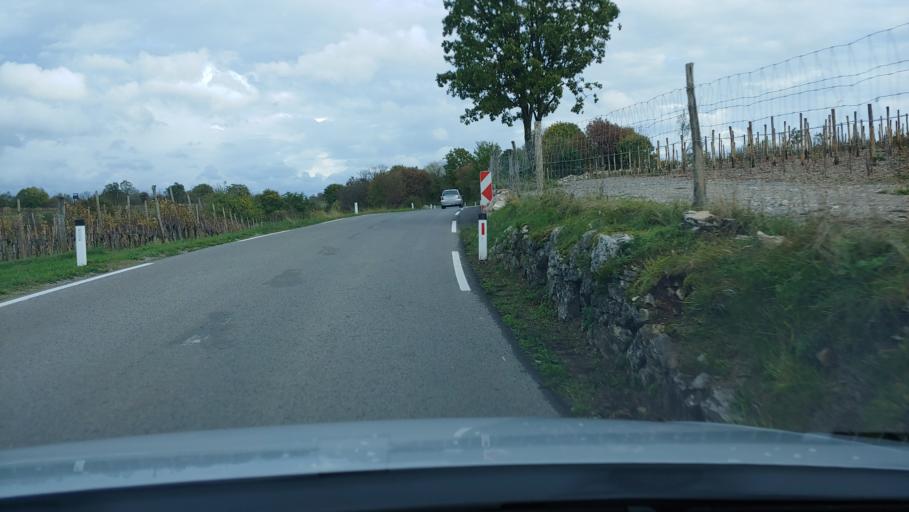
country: SI
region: Komen
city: Komen
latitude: 45.8062
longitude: 13.7193
